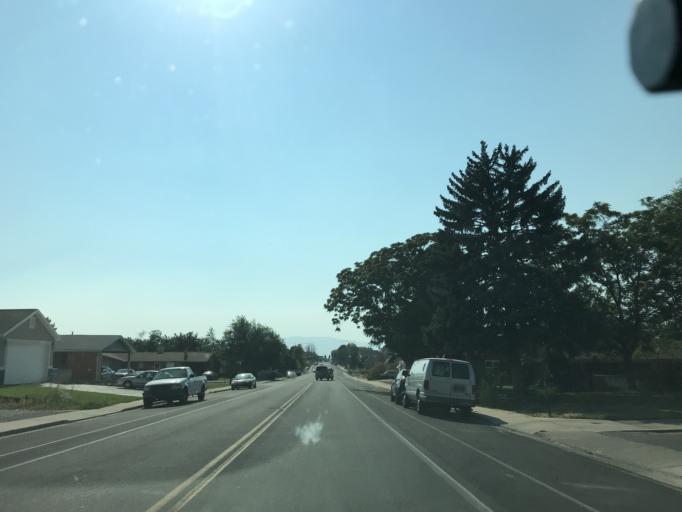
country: US
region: Utah
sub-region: Utah County
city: Orem
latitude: 40.2824
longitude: -111.6923
